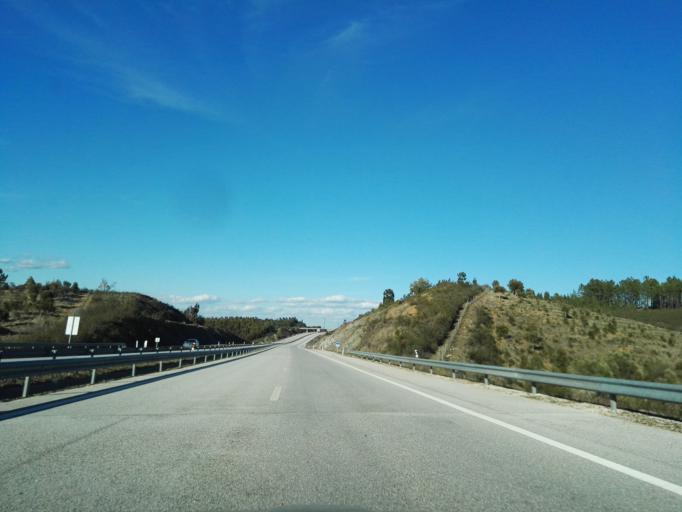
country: PT
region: Castelo Branco
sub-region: Castelo Branco
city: Castelo Branco
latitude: 39.7963
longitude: -7.5613
